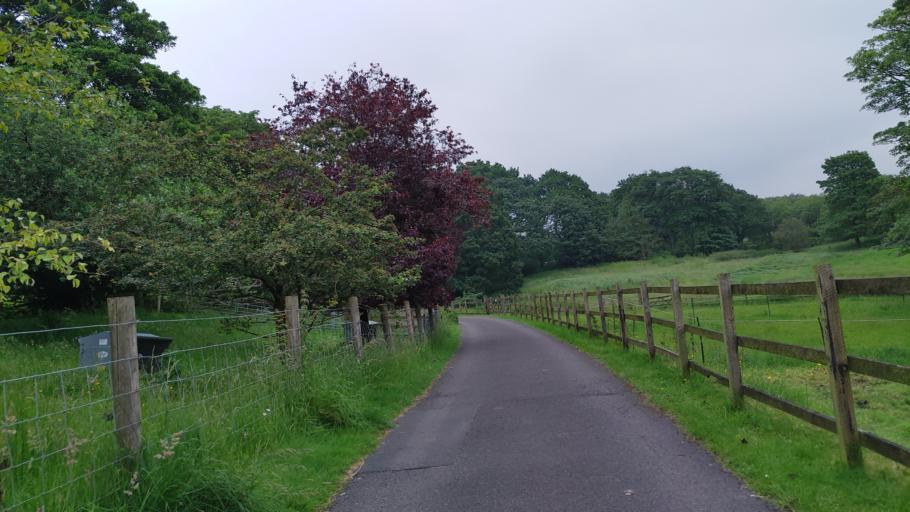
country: GB
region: England
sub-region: Lancashire
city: Chorley
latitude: 53.6806
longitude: -2.5818
